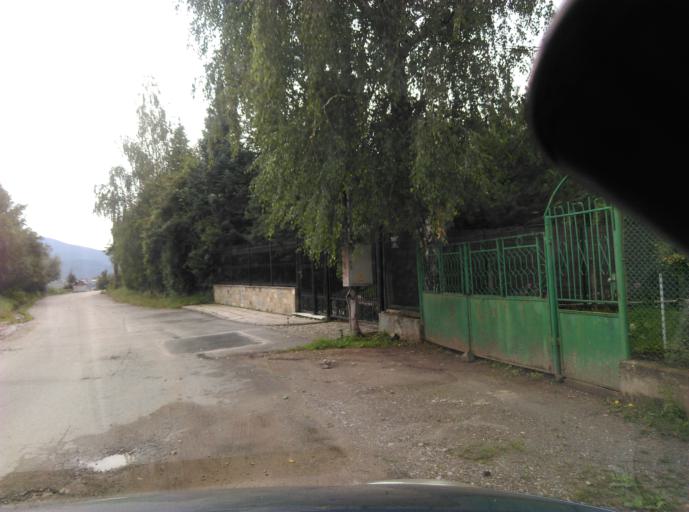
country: BG
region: Sofia-Capital
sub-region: Stolichna Obshtina
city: Sofia
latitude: 42.6025
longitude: 23.3984
